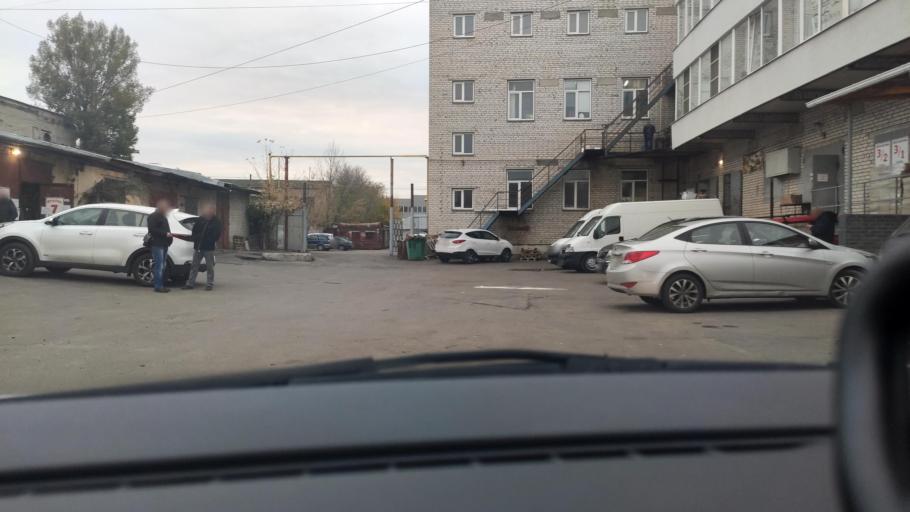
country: RU
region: Voronezj
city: Voronezh
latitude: 51.6651
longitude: 39.1563
